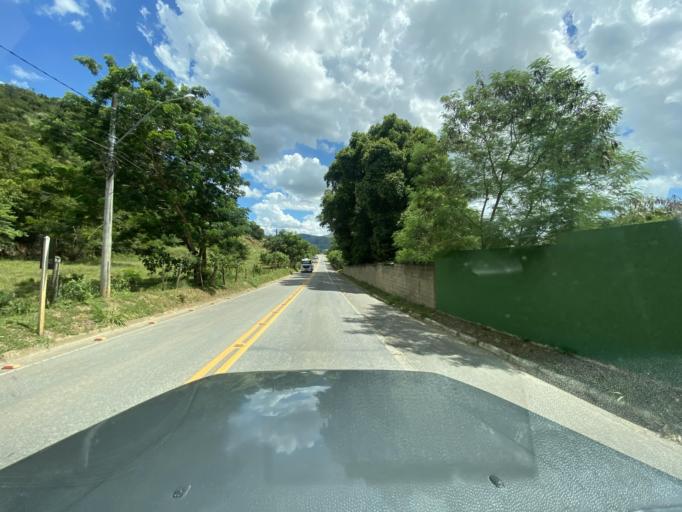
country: BR
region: Espirito Santo
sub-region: Jeronimo Monteiro
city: Jeronimo Monteiro
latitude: -20.7915
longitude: -41.3946
